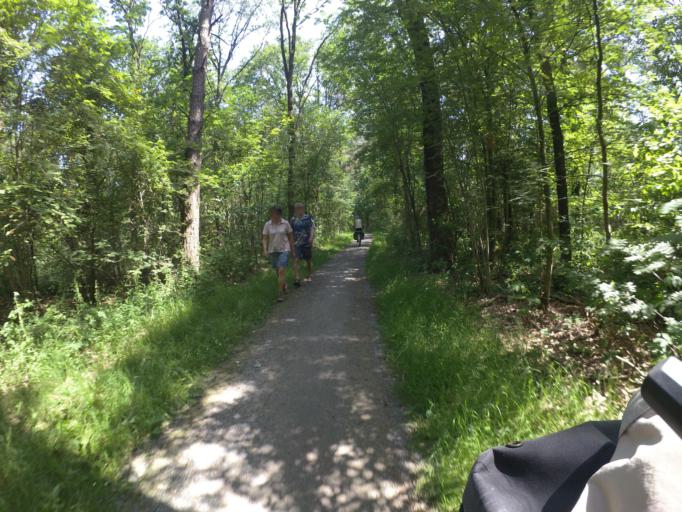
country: NL
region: Drenthe
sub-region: Gemeente De Wolden
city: Ruinen
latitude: 52.7466
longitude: 6.4012
